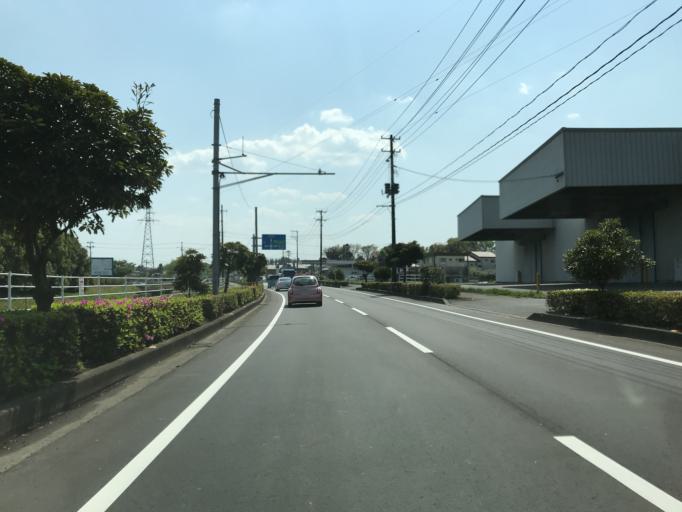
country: JP
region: Ibaraki
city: Kitaibaraki
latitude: 36.9011
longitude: 140.7683
